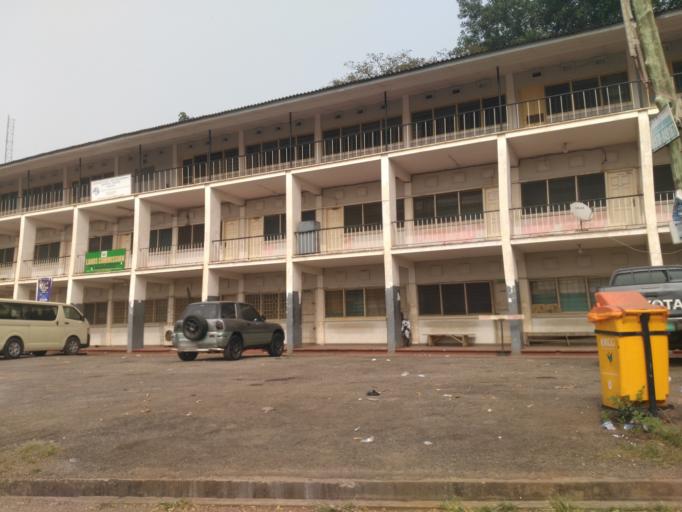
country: GH
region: Ashanti
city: Kumasi
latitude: 6.6902
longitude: -1.6240
